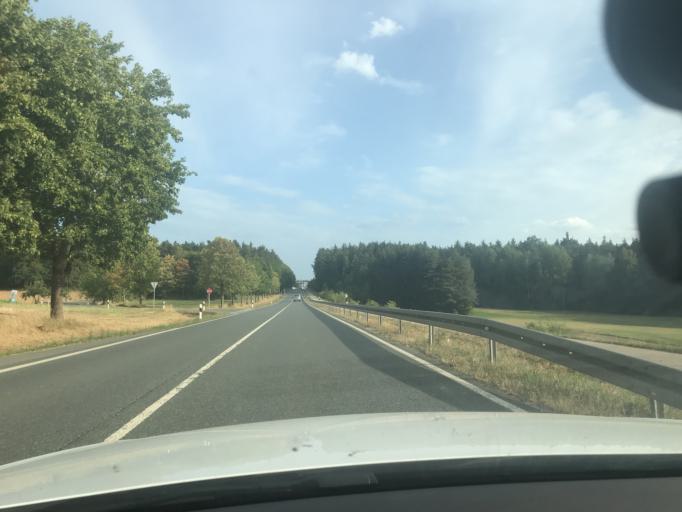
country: DE
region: Bavaria
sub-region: Upper Franconia
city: Emtmannsberg
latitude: 49.9000
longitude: 11.6094
